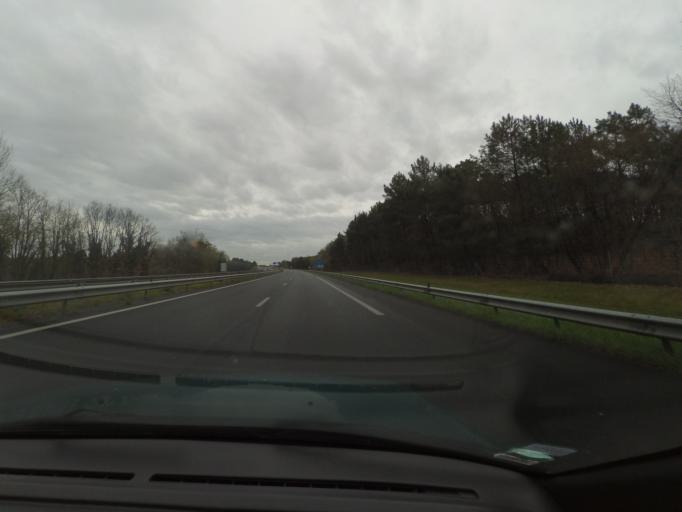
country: FR
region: Pays de la Loire
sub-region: Departement de Maine-et-Loire
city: Baune
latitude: 47.5315
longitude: -0.3441
